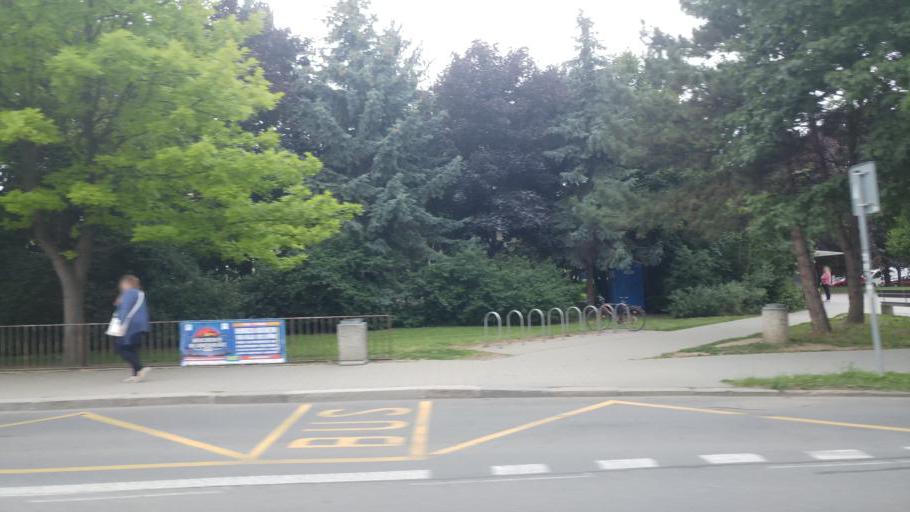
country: CZ
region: Central Bohemia
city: Roztoky
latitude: 50.1328
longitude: 14.3776
